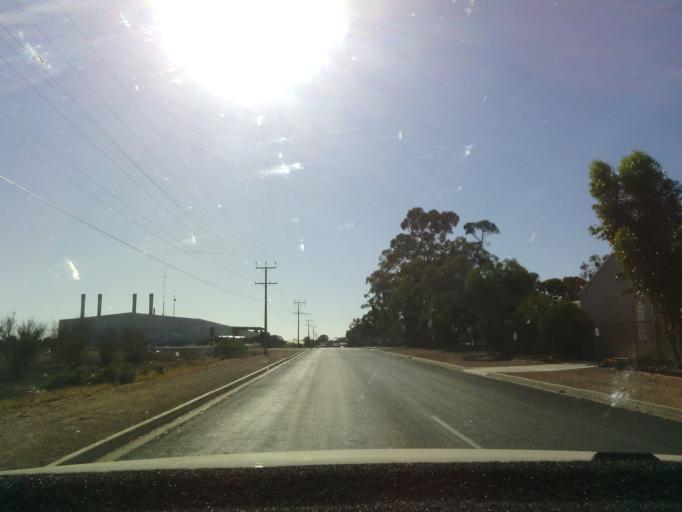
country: AU
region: South Australia
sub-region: Berri and Barmera
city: Berri
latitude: -34.2714
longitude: 140.5971
